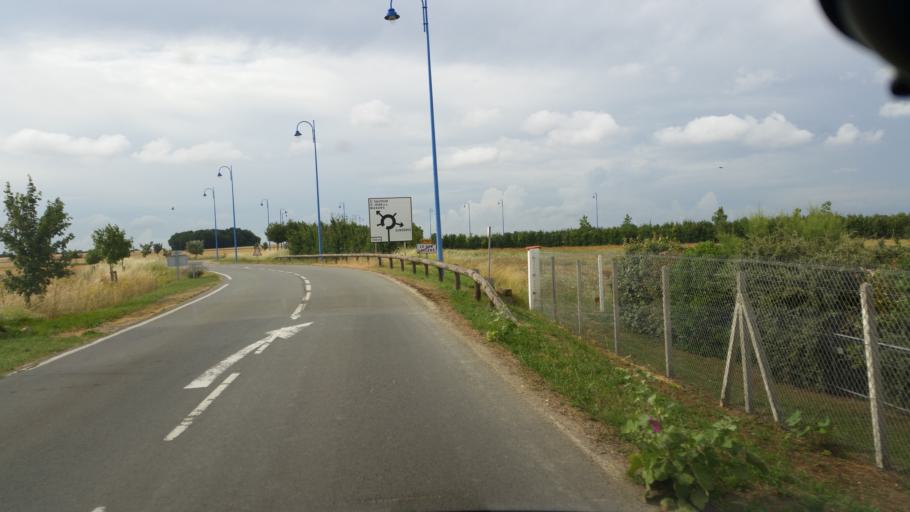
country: FR
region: Poitou-Charentes
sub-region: Departement de la Charente-Maritime
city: Courcon
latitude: 46.1939
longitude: -0.8675
